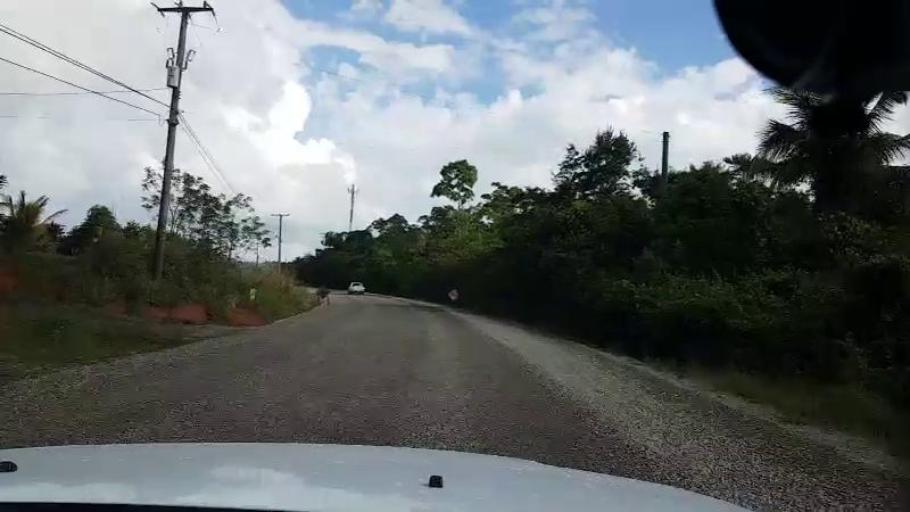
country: BZ
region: Cayo
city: Belmopan
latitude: 17.0884
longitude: -88.6173
